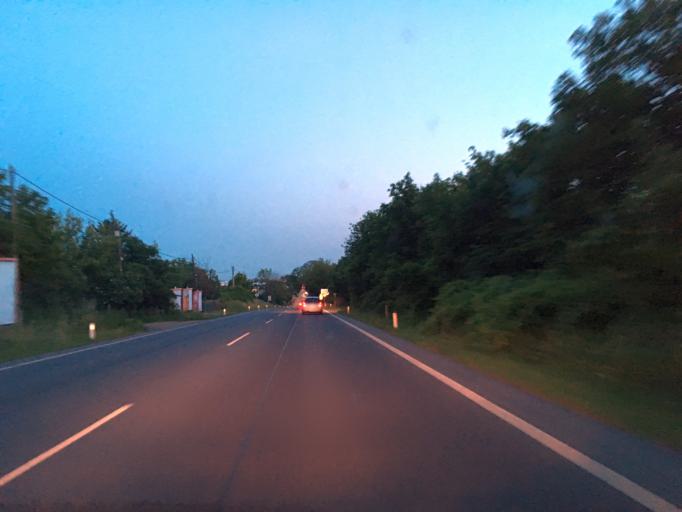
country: AT
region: Lower Austria
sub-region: Politischer Bezirk Korneuburg
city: Hagenbrunn
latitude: 48.3057
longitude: 16.4253
